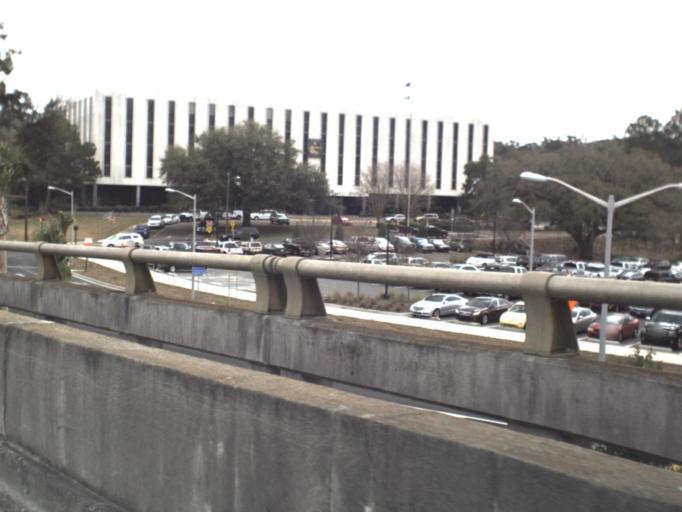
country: US
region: Florida
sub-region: Leon County
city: Tallahassee
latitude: 30.4380
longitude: -84.2763
